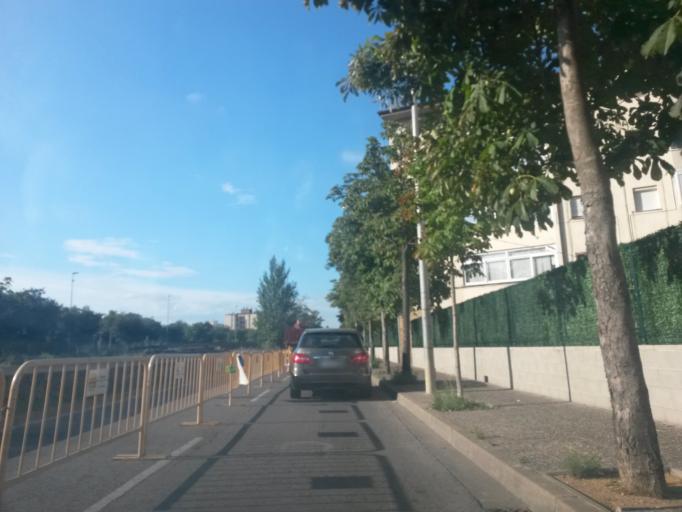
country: ES
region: Catalonia
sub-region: Provincia de Girona
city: Salt
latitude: 41.9756
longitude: 2.8093
